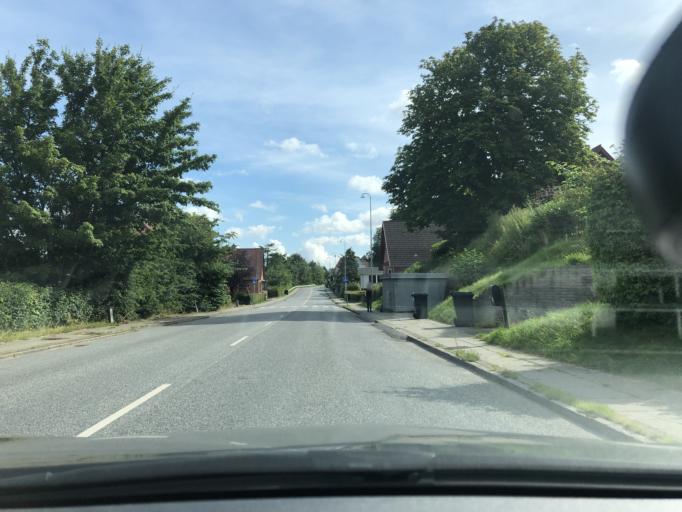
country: DK
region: South Denmark
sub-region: Vejle Kommune
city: Vejle
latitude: 55.7009
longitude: 9.5155
